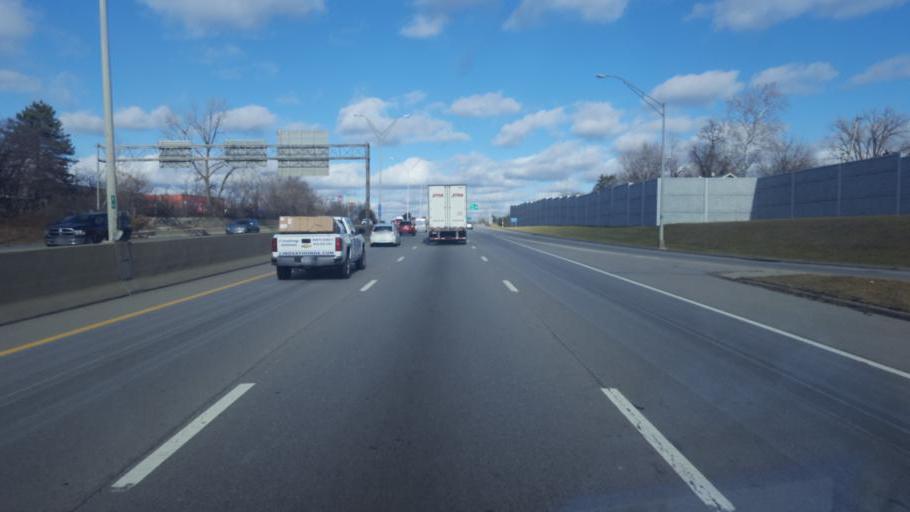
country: US
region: Ohio
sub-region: Franklin County
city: Columbus
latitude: 39.9953
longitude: -82.9849
